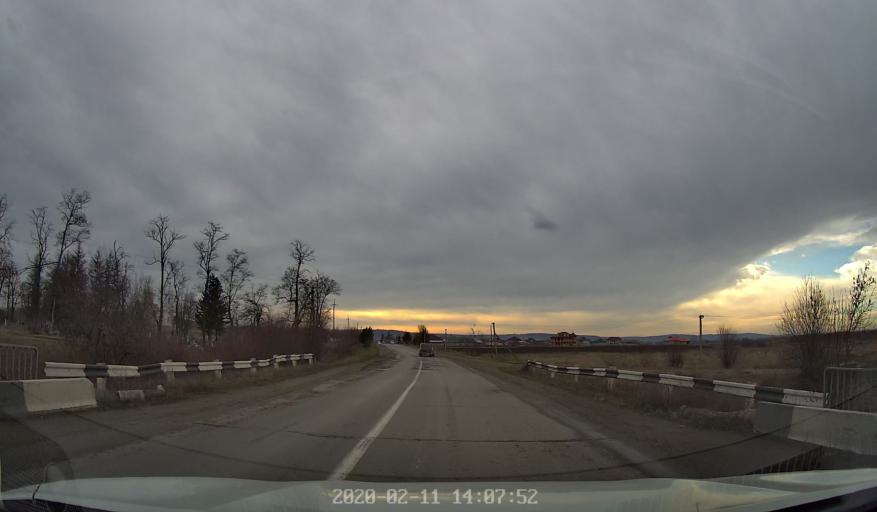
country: RO
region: Botosani
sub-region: Comuna Darabani
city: Bajura
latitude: 48.2430
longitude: 26.5489
